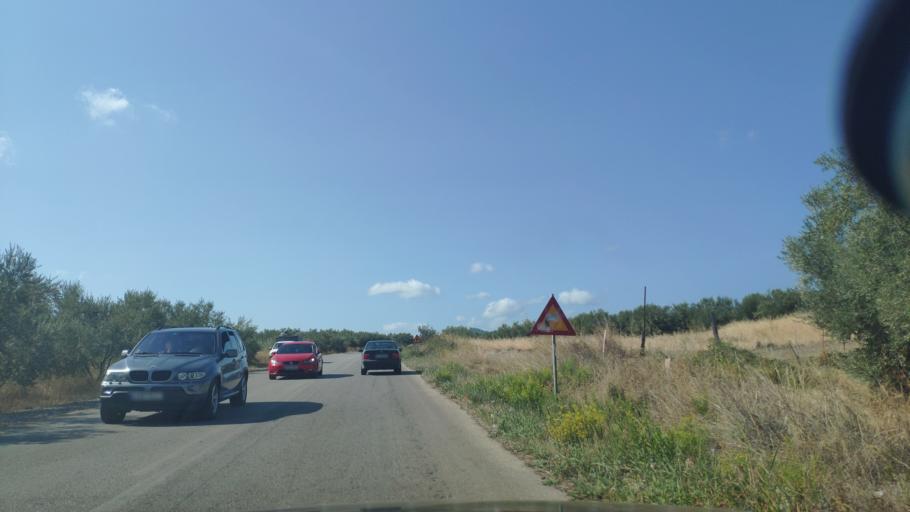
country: GR
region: Peloponnese
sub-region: Nomos Korinthias
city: Moulki
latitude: 37.9919
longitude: 22.6990
